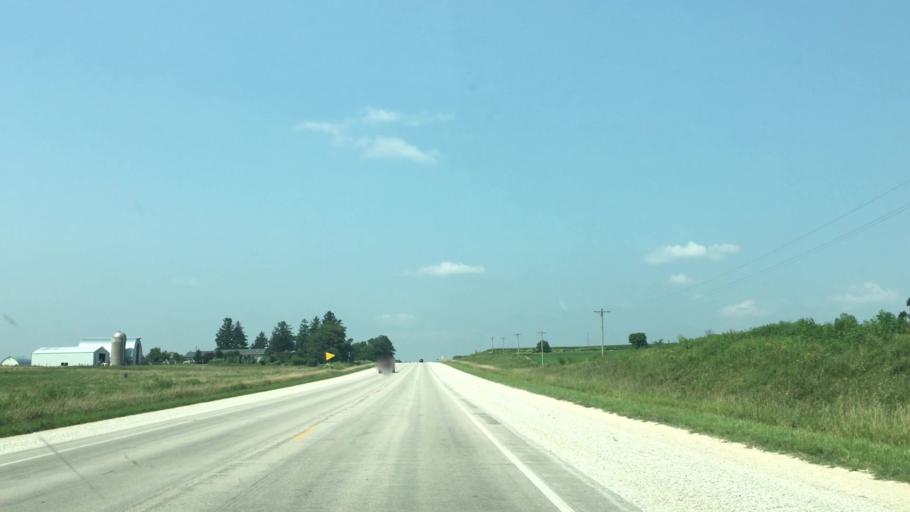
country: US
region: Iowa
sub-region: Winneshiek County
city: Decorah
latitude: 43.4173
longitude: -91.8592
